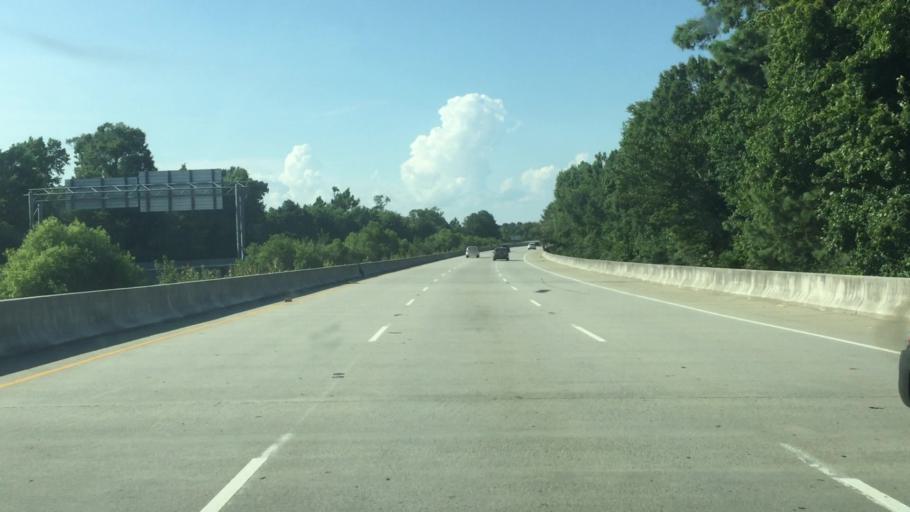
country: US
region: South Carolina
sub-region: Horry County
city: North Myrtle Beach
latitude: 33.7947
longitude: -78.7785
